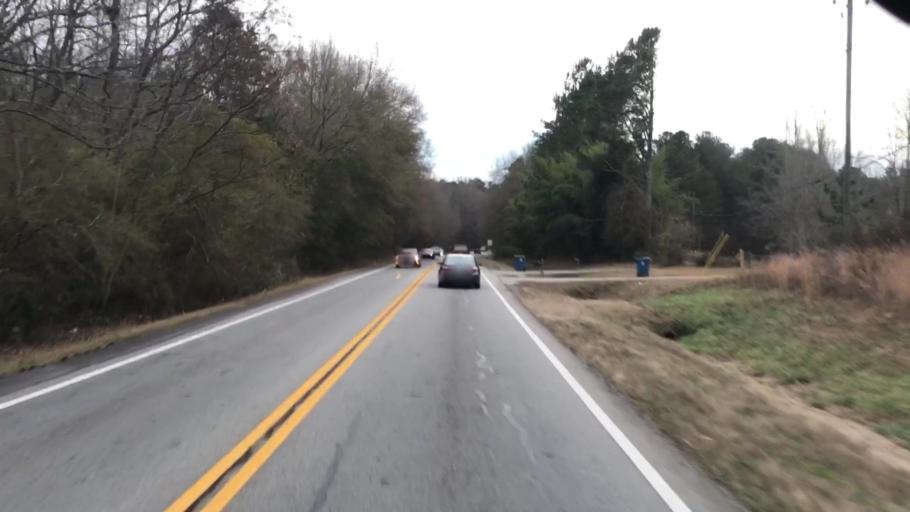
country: US
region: Georgia
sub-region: Barrow County
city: Auburn
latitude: 34.0388
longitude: -83.7751
